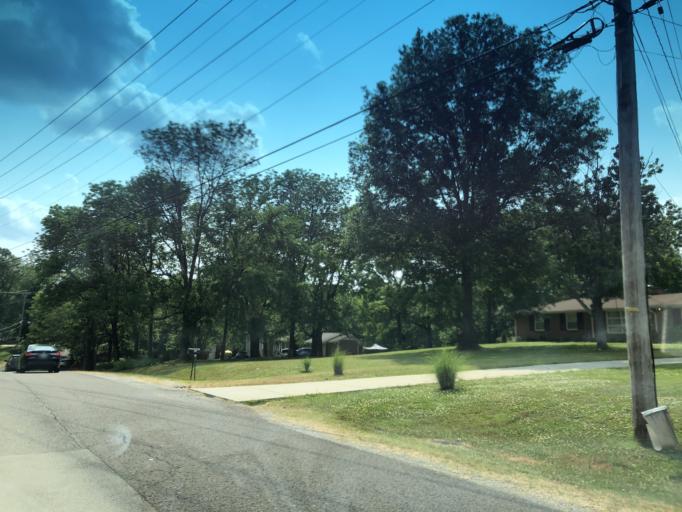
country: US
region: Tennessee
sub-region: Davidson County
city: Goodlettsville
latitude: 36.2557
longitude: -86.7316
